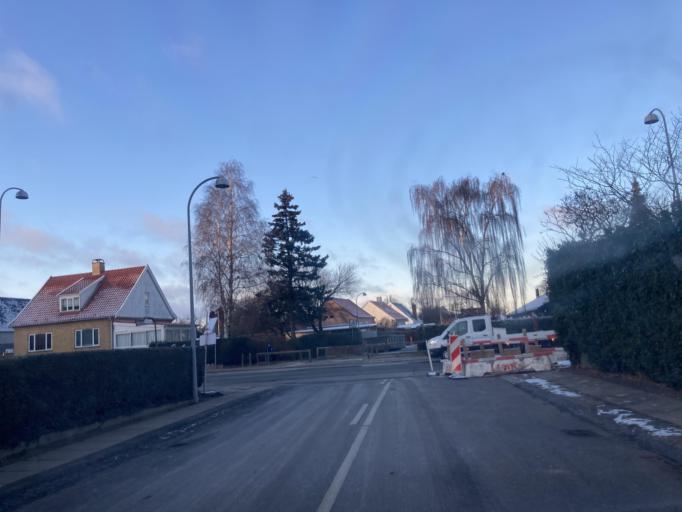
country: DK
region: Capital Region
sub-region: Hvidovre Kommune
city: Hvidovre
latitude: 55.6378
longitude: 12.4815
